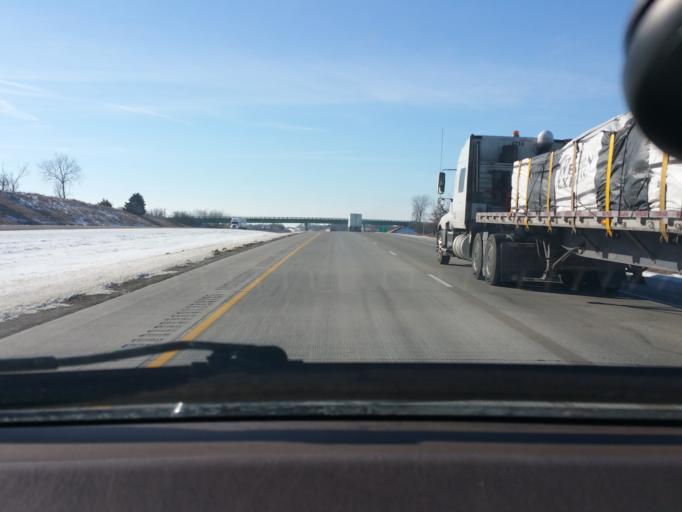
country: US
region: Iowa
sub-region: Decatur County
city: Lamoni
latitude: 40.6407
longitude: -93.8726
